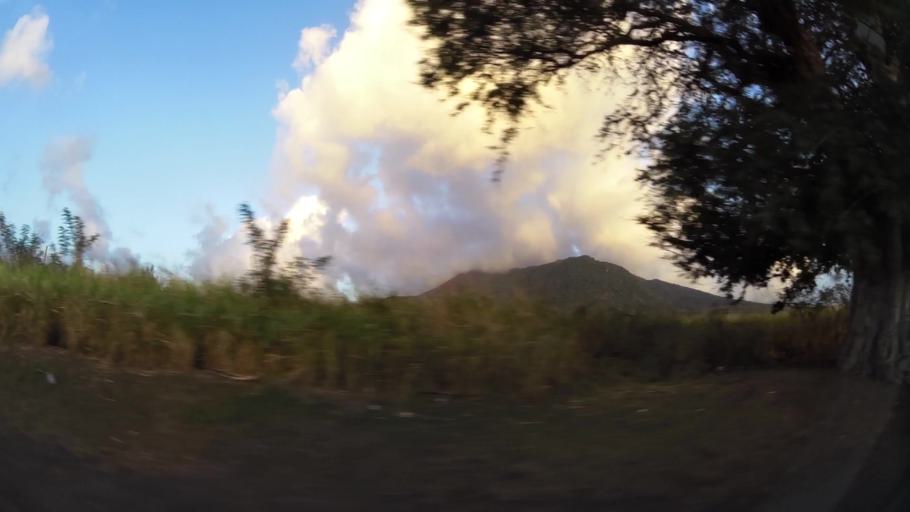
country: KN
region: Saint Anne Sandy Point
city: Sandy Point Town
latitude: 17.3714
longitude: -62.8525
